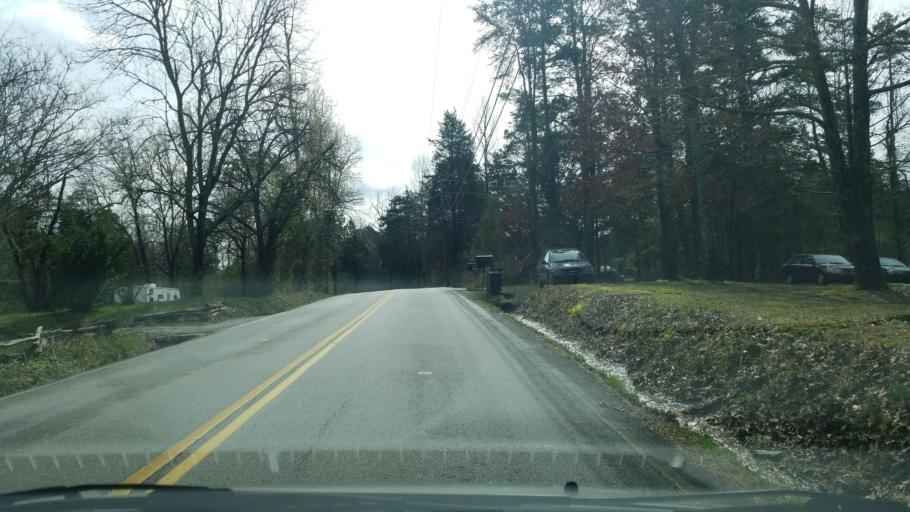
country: US
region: Tennessee
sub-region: Hamilton County
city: Harrison
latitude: 35.1398
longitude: -85.0895
